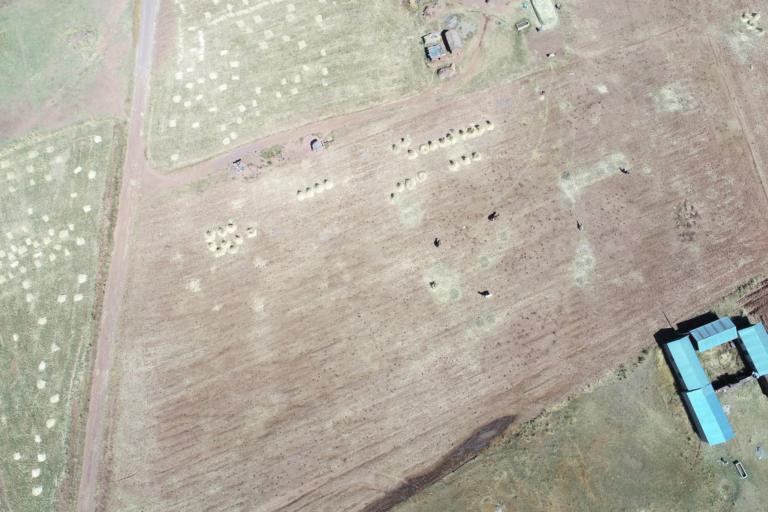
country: BO
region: La Paz
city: Tiahuanaco
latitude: -16.5899
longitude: -68.7714
